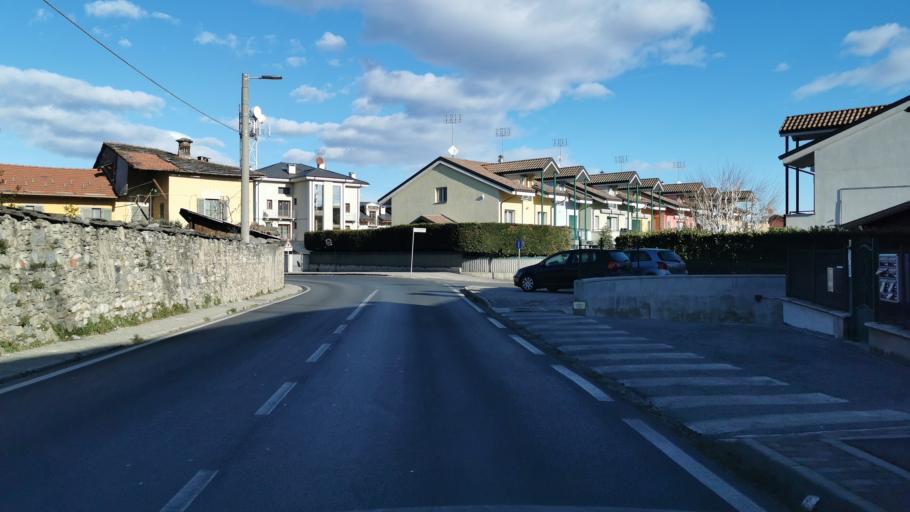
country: IT
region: Piedmont
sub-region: Provincia di Cuneo
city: Caraglio
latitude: 44.4204
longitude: 7.4326
